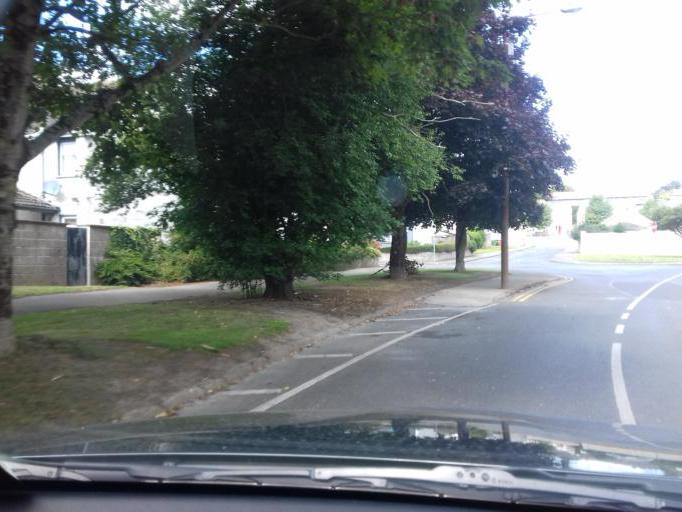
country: IE
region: Munster
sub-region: Waterford
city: Waterford
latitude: 52.2496
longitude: -7.1245
